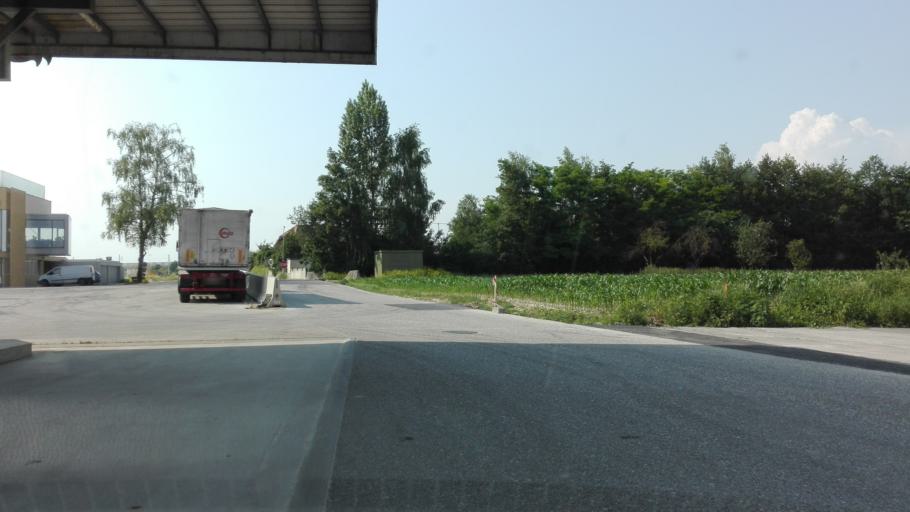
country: AT
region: Upper Austria
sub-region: Politischer Bezirk Linz-Land
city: Horsching
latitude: 48.1990
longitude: 14.1615
